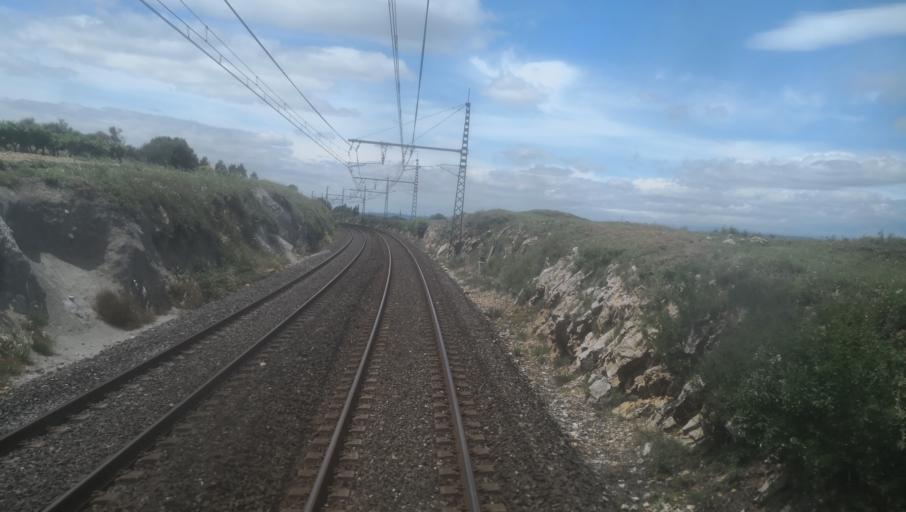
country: FR
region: Languedoc-Roussillon
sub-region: Departement de l'Aude
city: Nevian
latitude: 43.2128
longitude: 2.8911
